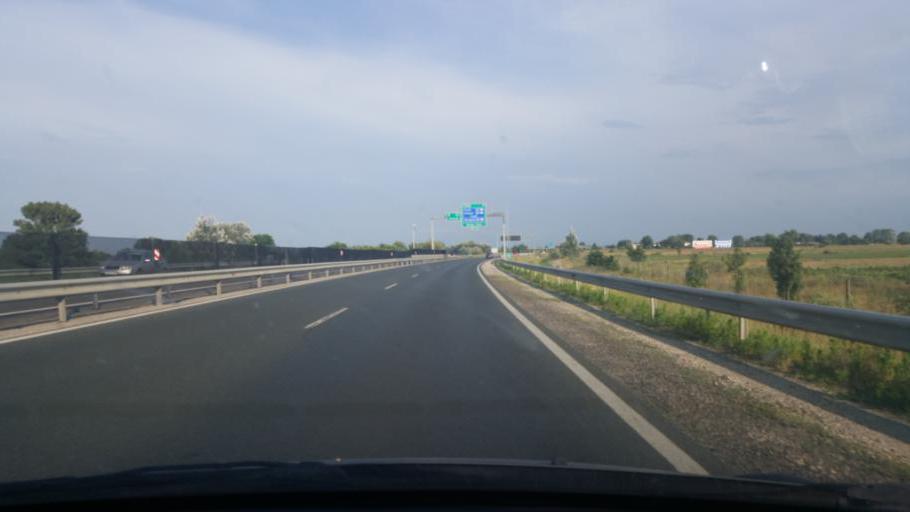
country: HU
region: Pest
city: Vecses
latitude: 47.4122
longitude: 19.2927
